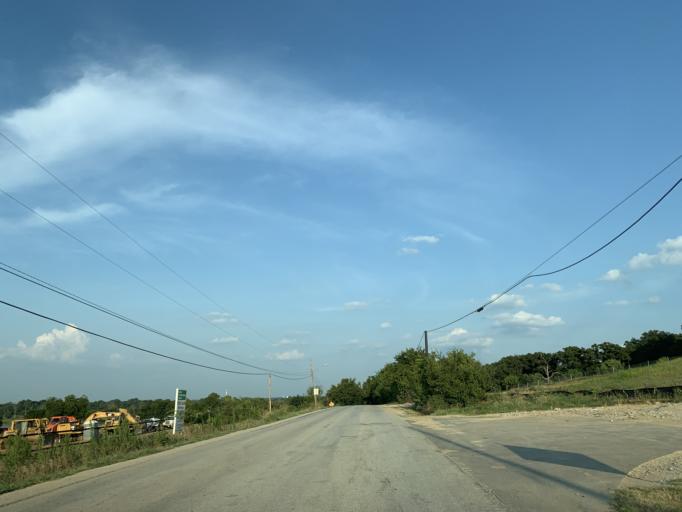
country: US
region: Texas
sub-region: Tarrant County
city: Hurst
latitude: 32.7814
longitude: -97.1922
